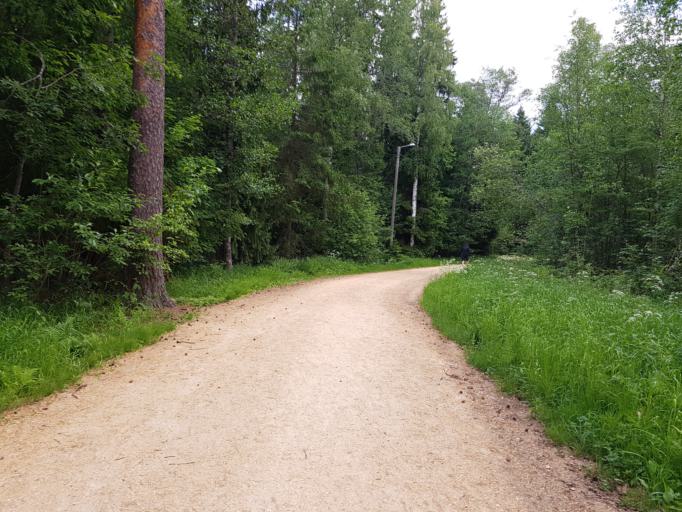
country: FI
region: Uusimaa
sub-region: Helsinki
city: Helsinki
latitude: 60.2596
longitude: 24.9141
